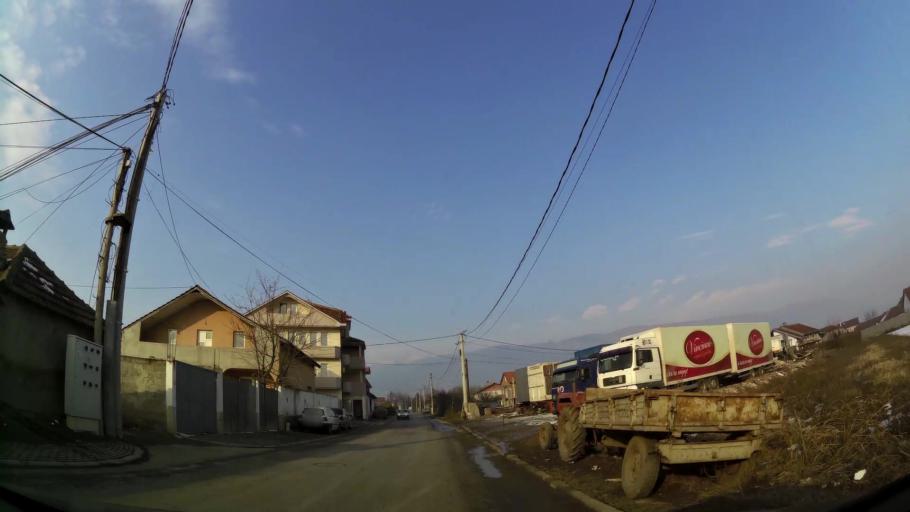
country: MK
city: Creshevo
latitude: 42.0212
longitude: 21.5147
